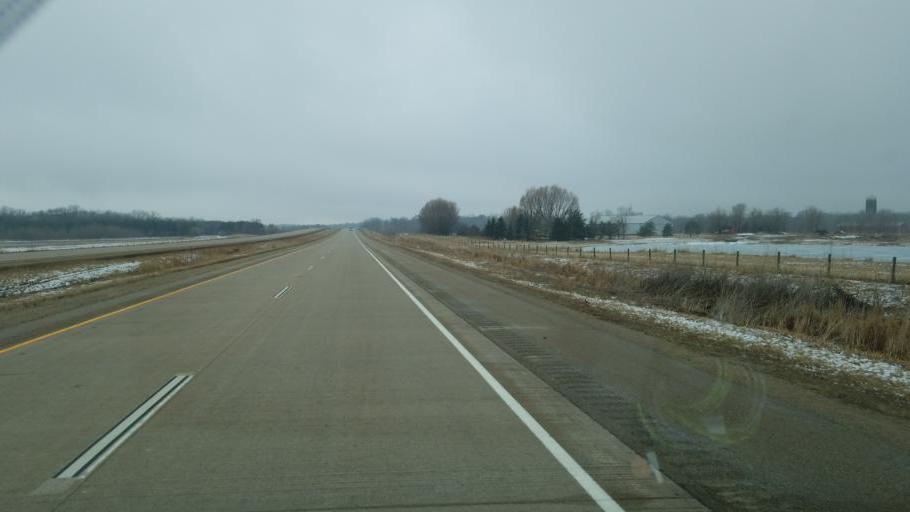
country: US
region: Wisconsin
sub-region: Winnebago County
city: Winneconne
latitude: 44.2403
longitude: -88.7904
